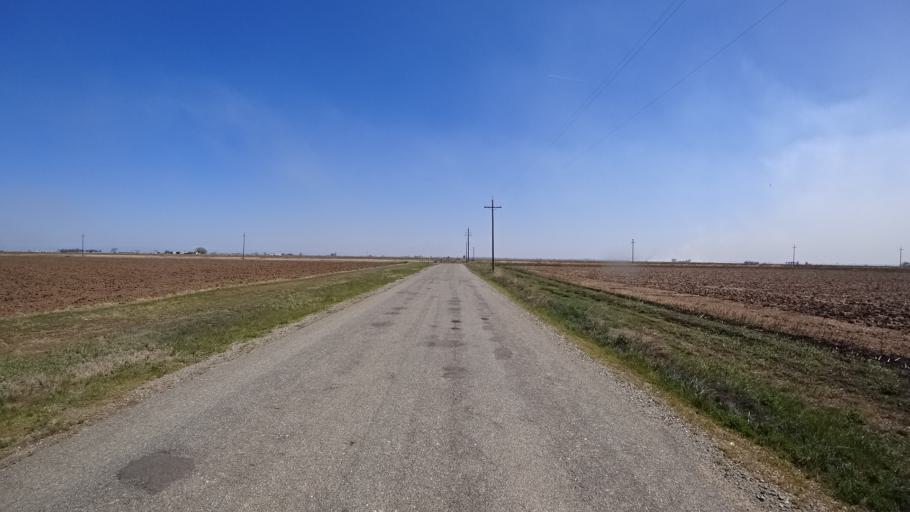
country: US
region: California
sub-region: Glenn County
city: Willows
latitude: 39.3998
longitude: -122.2501
